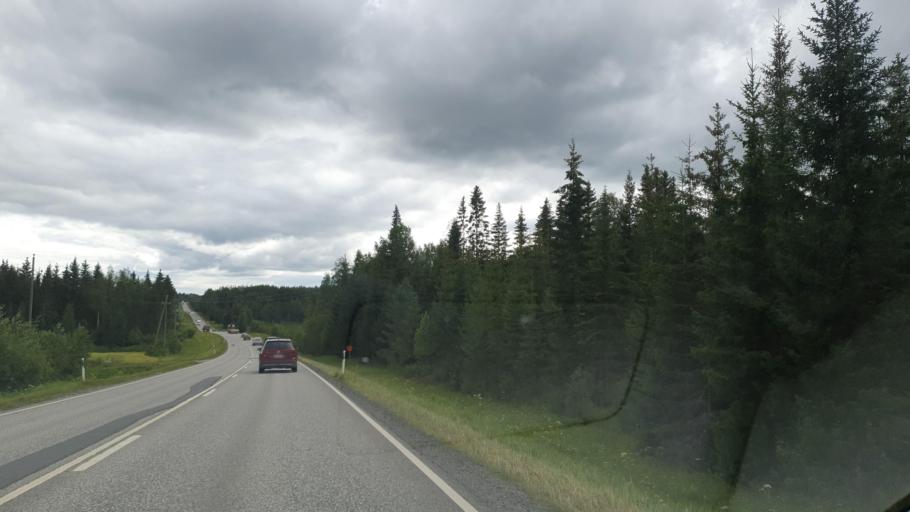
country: FI
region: Northern Savo
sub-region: Ylae-Savo
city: Sonkajaervi
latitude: 63.7109
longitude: 27.3595
